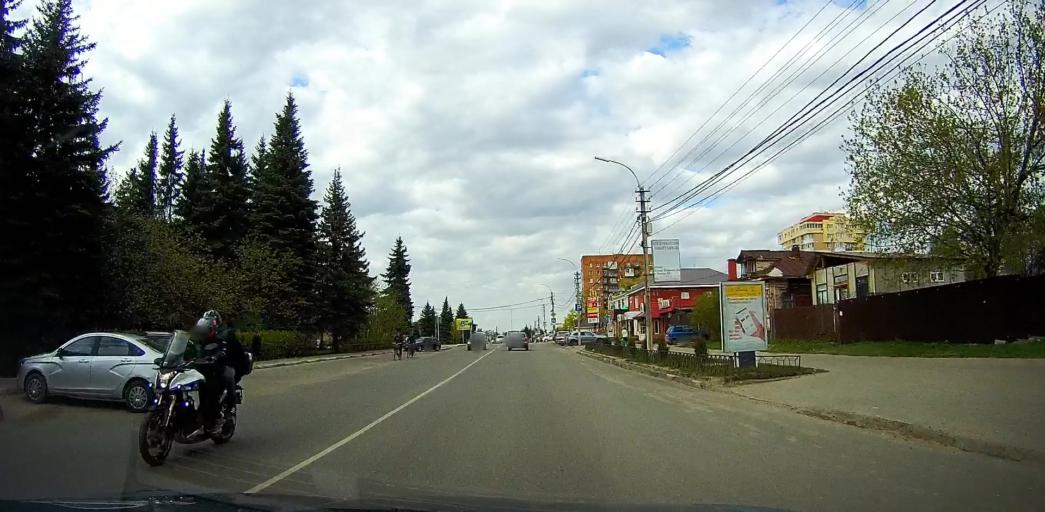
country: RU
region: Moskovskaya
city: Pavlovskiy Posad
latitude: 55.7770
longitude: 38.6517
